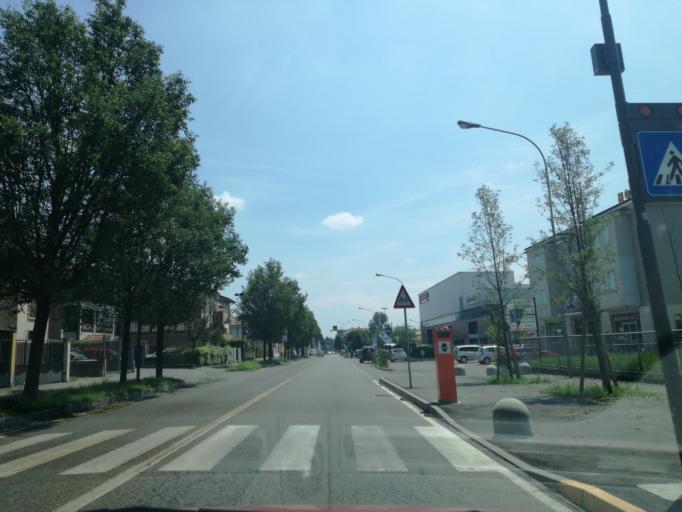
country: IT
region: Lombardy
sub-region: Provincia di Monza e Brianza
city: Desio
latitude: 45.6290
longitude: 9.2057
